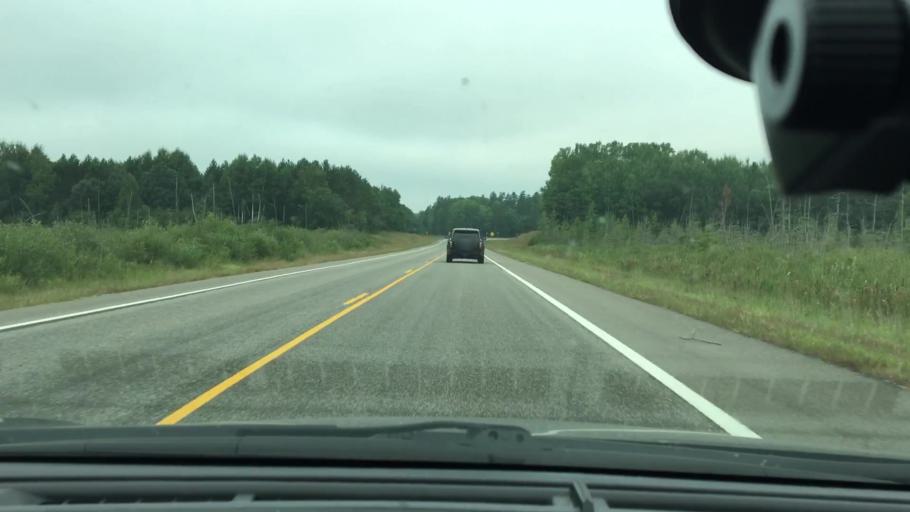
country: US
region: Minnesota
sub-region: Crow Wing County
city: Cross Lake
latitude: 46.6601
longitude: -94.0289
